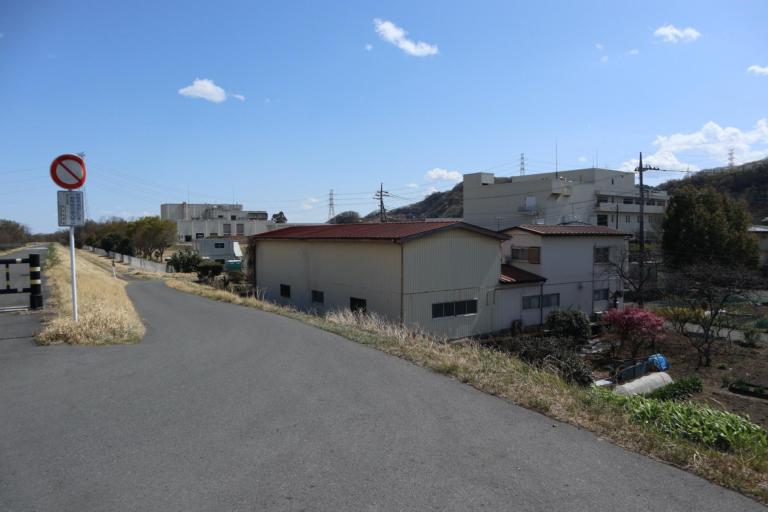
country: JP
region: Gunma
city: Kiryu
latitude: 36.3663
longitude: 139.3669
